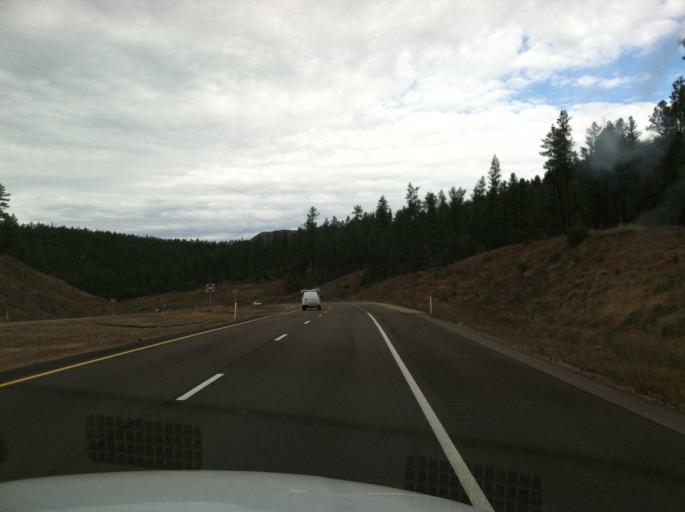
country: US
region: Arizona
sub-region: Gila County
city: Star Valley
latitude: 34.3277
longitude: -111.0879
